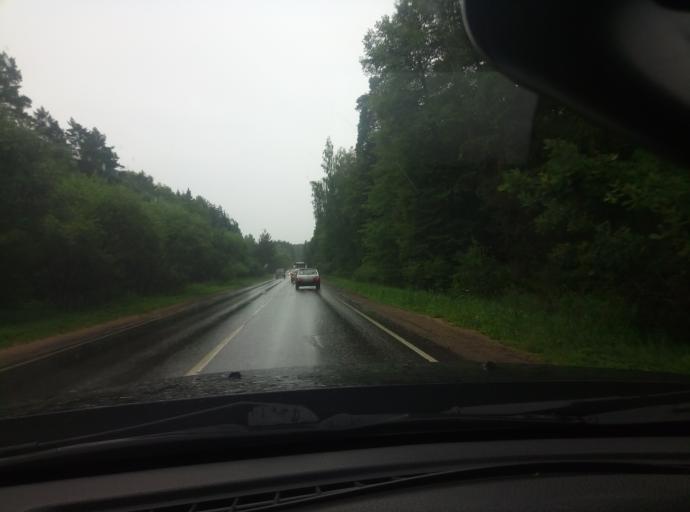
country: RU
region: Moskovskaya
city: Protvino
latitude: 54.8852
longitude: 37.1726
